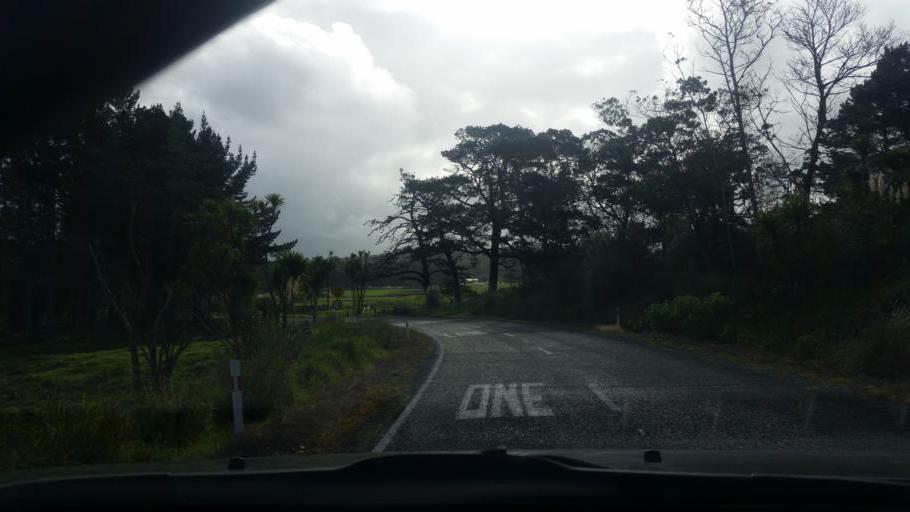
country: NZ
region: Auckland
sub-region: Auckland
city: Wellsford
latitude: -36.2421
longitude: 174.2302
